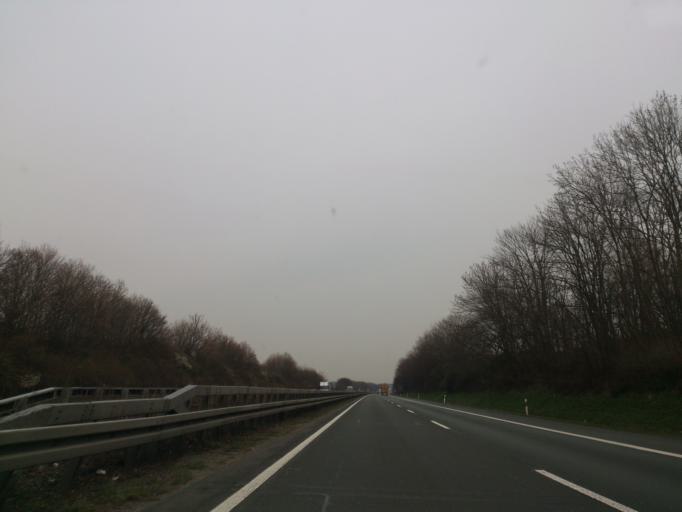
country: DE
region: North Rhine-Westphalia
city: Erwitte
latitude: 51.5893
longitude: 8.4121
